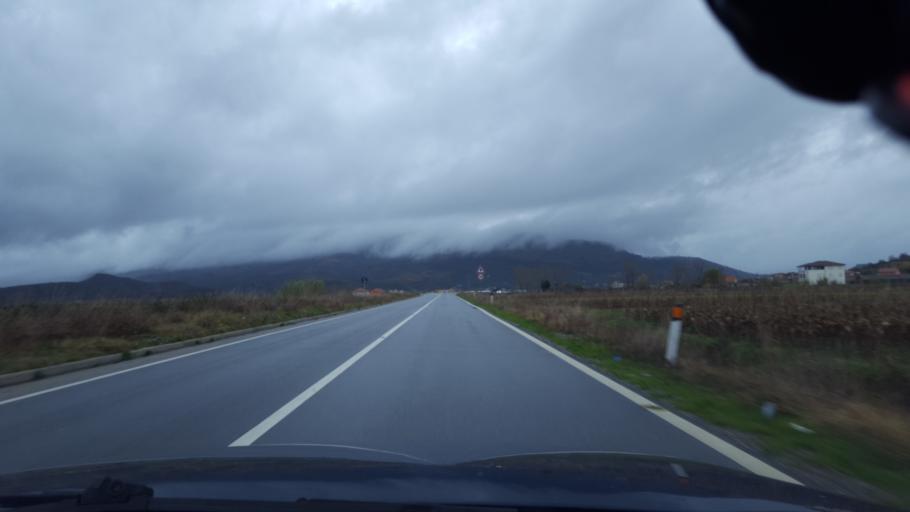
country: AL
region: Shkoder
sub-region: Rrethi i Shkodres
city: Berdica e Madhe
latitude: 42.0034
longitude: 19.4806
